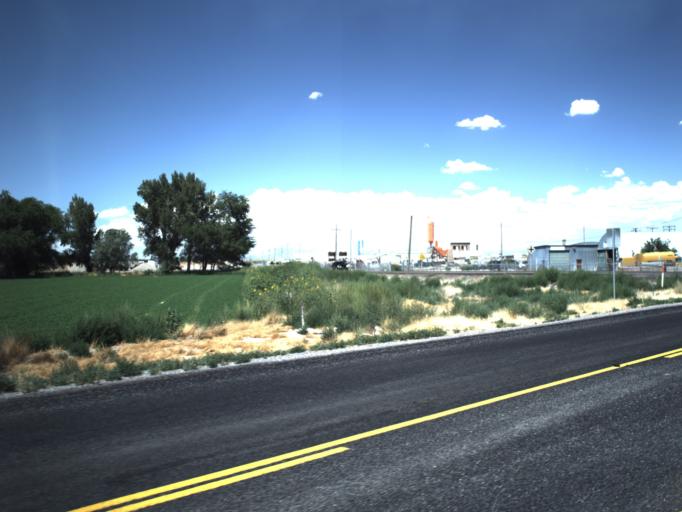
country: US
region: Utah
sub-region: Millard County
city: Delta
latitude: 39.3506
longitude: -112.5960
